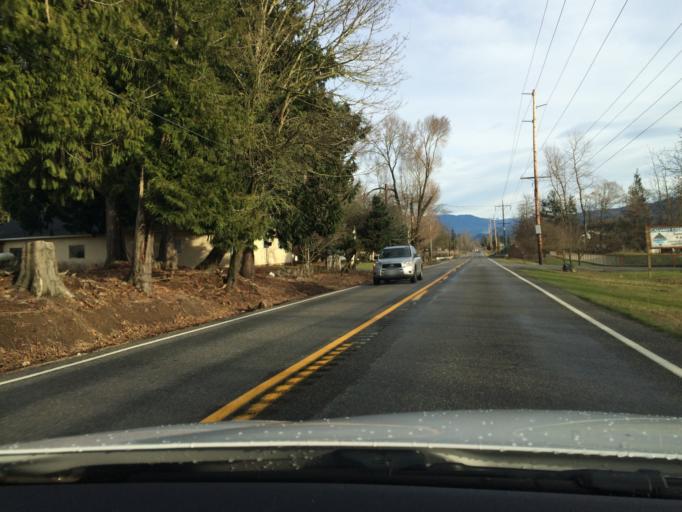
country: US
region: Washington
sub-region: Whatcom County
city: Everson
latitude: 48.9638
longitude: -122.3633
